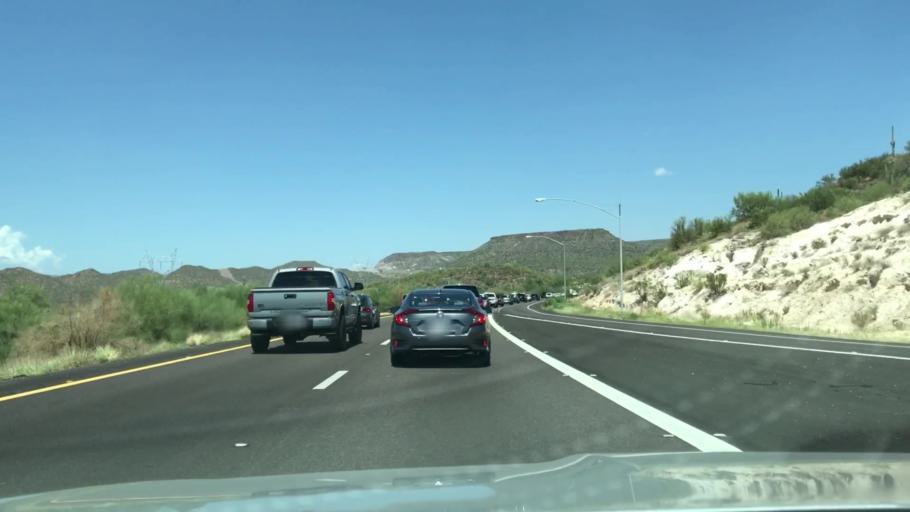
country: US
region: Arizona
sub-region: Yavapai County
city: Black Canyon City
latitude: 34.0872
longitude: -112.1428
